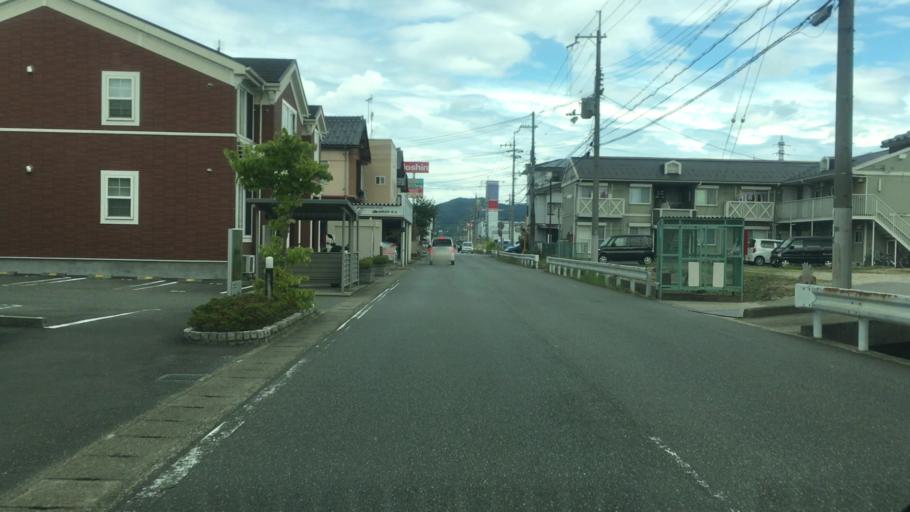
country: JP
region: Hyogo
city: Toyooka
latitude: 35.5517
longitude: 134.8130
